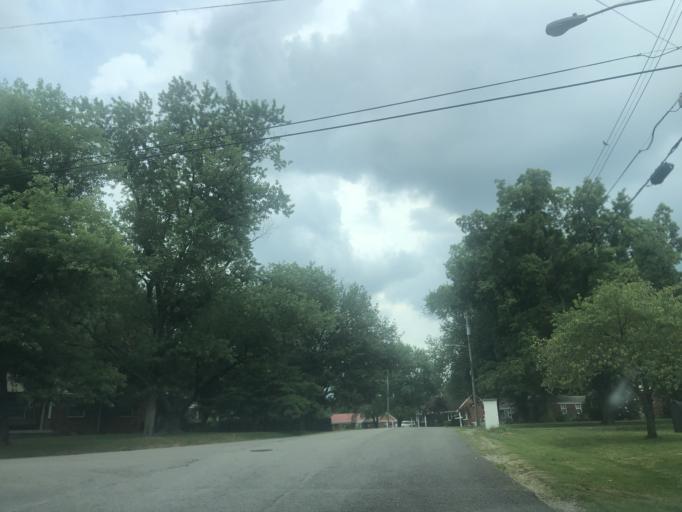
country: US
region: Tennessee
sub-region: Davidson County
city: Nashville
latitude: 36.1550
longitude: -86.6858
